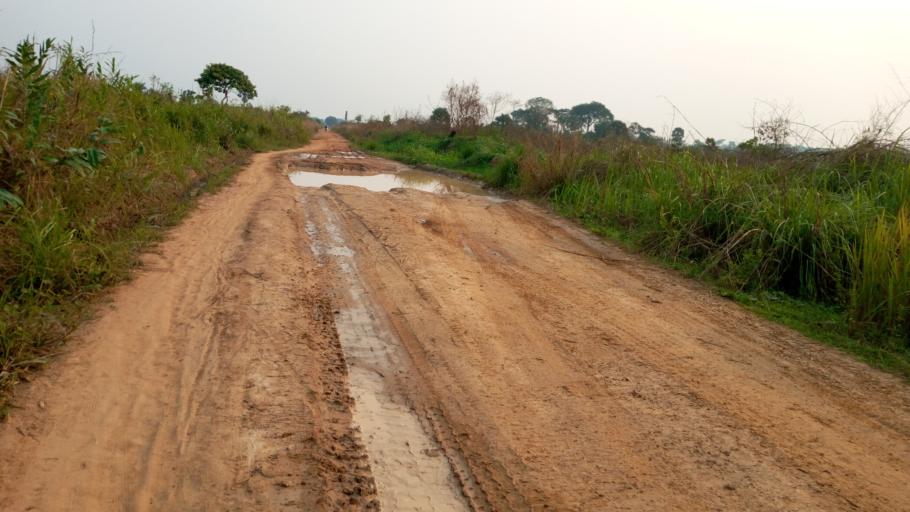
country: CD
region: Bandundu
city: Bandundu
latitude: -3.4223
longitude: 17.6098
